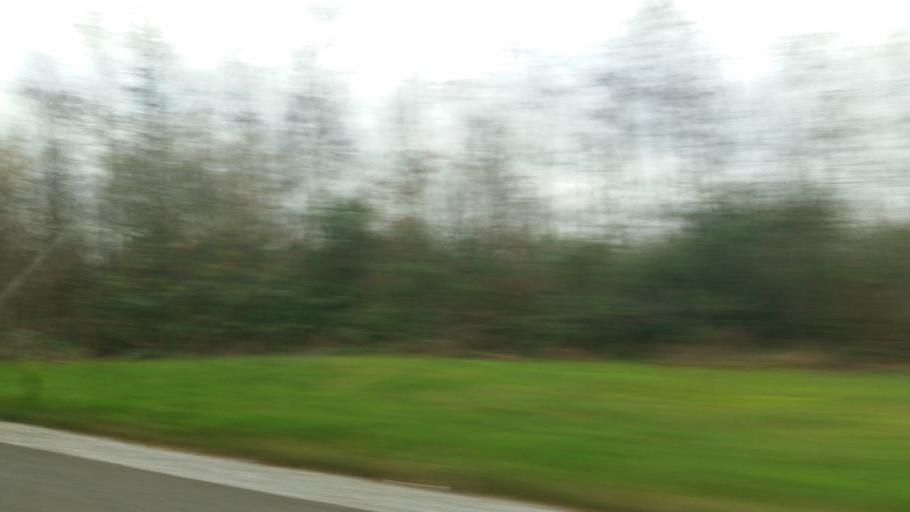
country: IE
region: Leinster
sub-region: Lu
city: Drogheda
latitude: 53.6724
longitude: -6.3505
